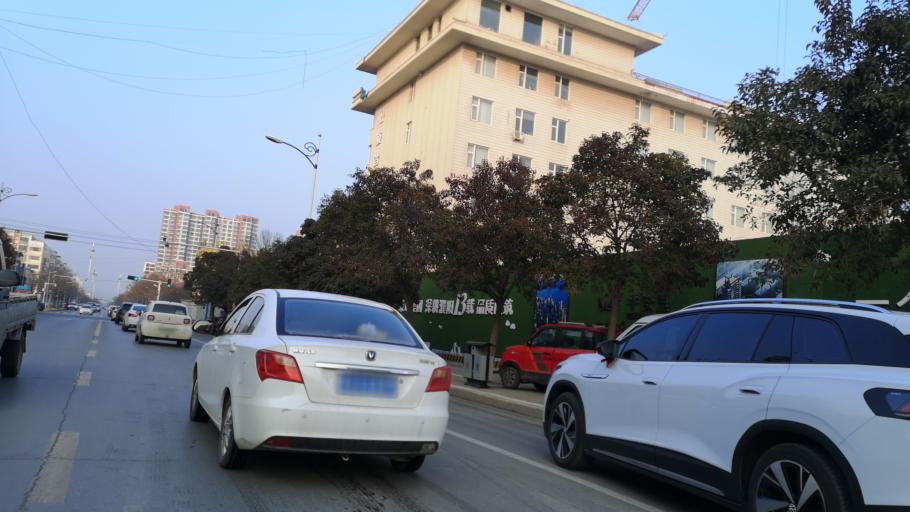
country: CN
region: Henan Sheng
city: Zhongyuanlu
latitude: 35.7689
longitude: 115.0636
